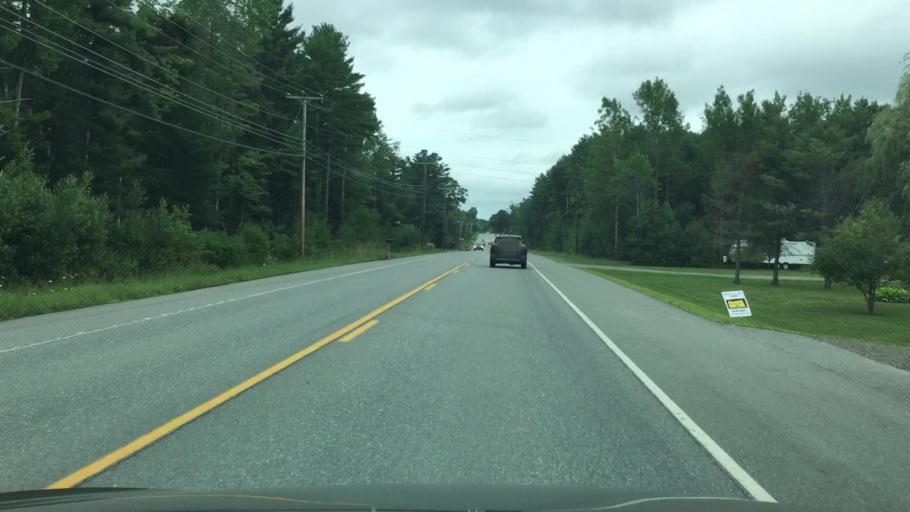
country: US
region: Maine
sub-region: Penobscot County
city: Orrington
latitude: 44.7054
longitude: -68.8232
